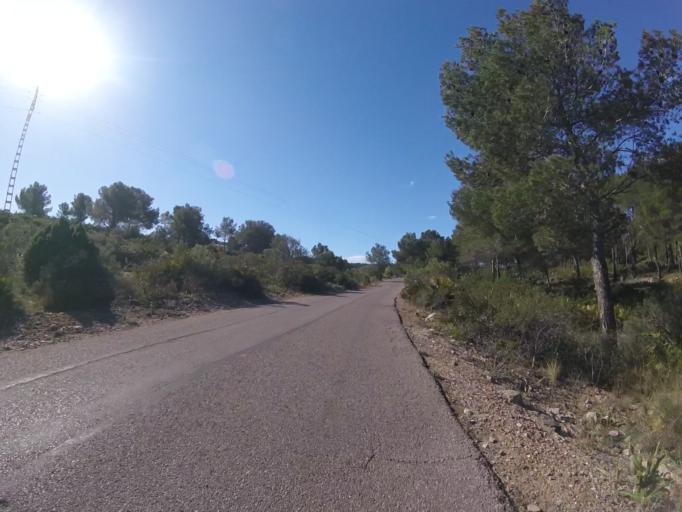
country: ES
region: Valencia
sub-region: Provincia de Castello
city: Orpesa/Oropesa del Mar
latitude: 40.0871
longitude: 0.1248
